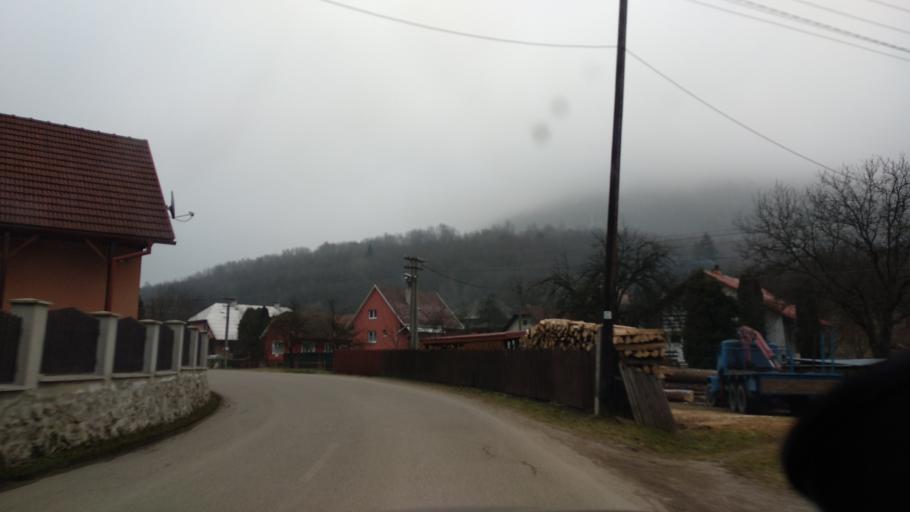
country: SK
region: Nitriansky
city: Ilava
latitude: 48.9022
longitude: 18.2693
